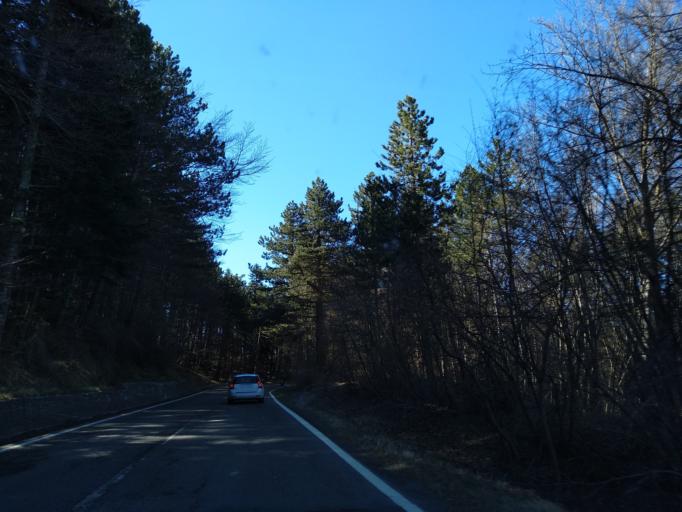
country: IT
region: Emilia-Romagna
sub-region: Provincia di Reggio Emilia
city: Busana
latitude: 44.4104
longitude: 10.3443
